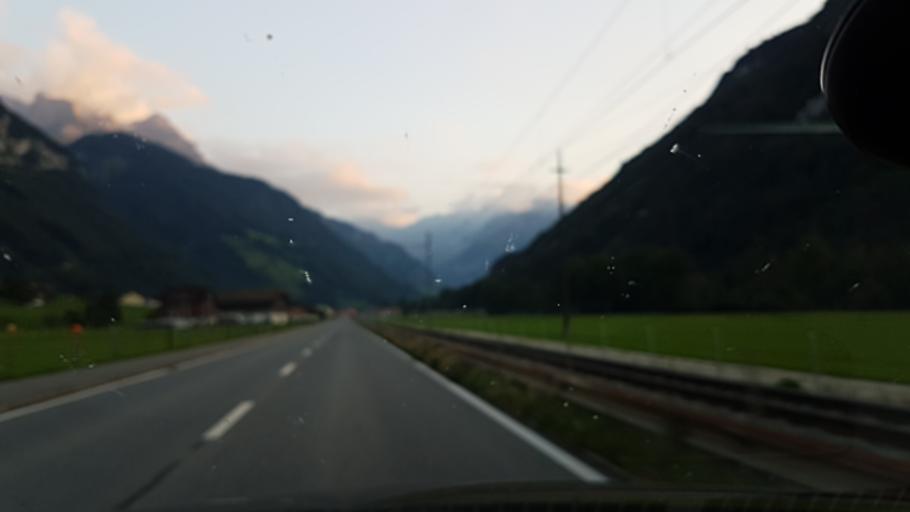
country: CH
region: Nidwalden
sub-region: Nidwalden
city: Dallenwil
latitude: 46.9182
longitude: 8.3968
